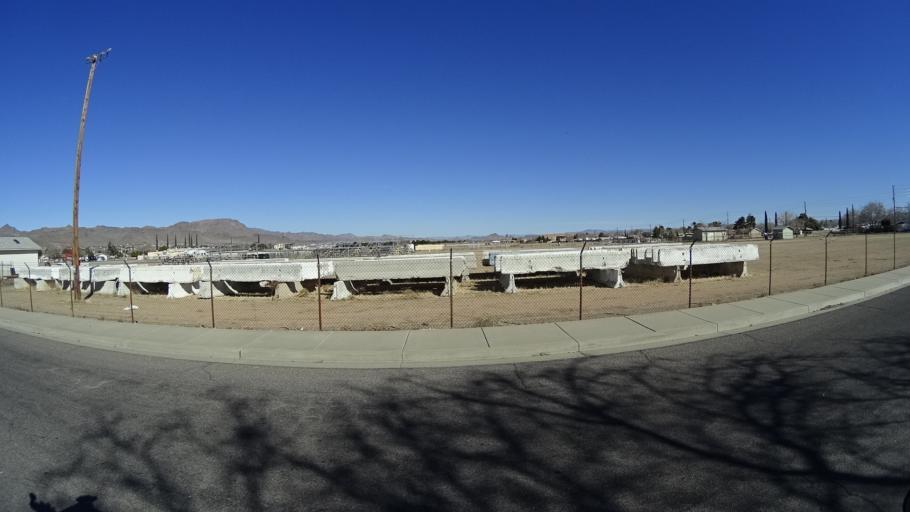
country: US
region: Arizona
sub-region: Mohave County
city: Kingman
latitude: 35.2088
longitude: -114.0260
